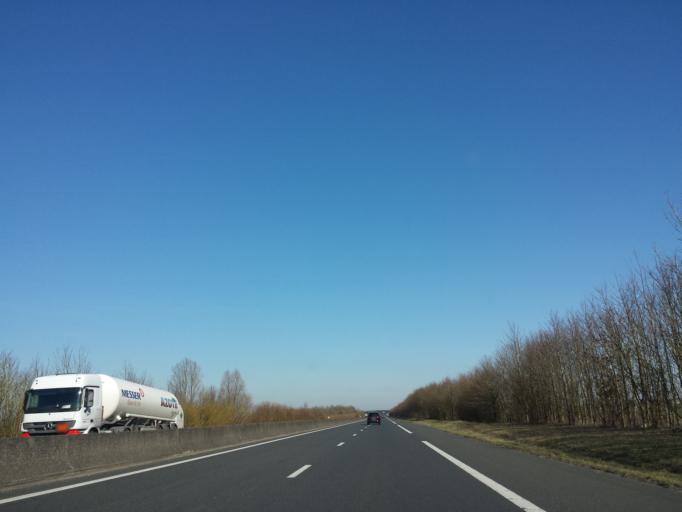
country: FR
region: Picardie
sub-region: Departement de l'Oise
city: Tille
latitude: 49.4757
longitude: 2.1634
